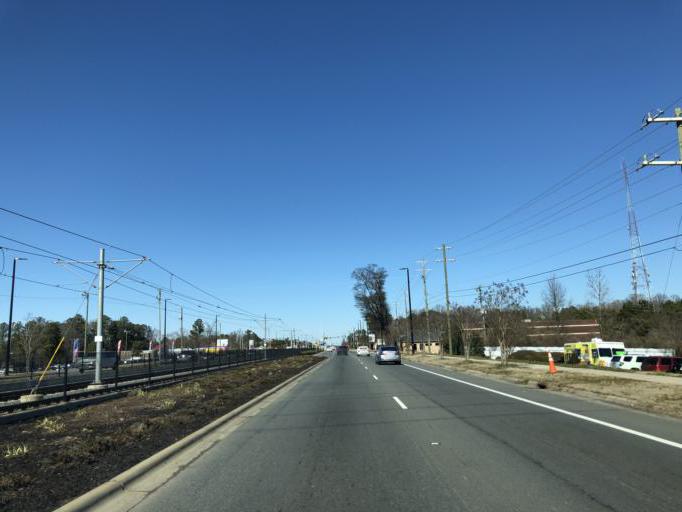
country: US
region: North Carolina
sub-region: Mecklenburg County
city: Charlotte
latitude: 35.2685
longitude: -80.7680
